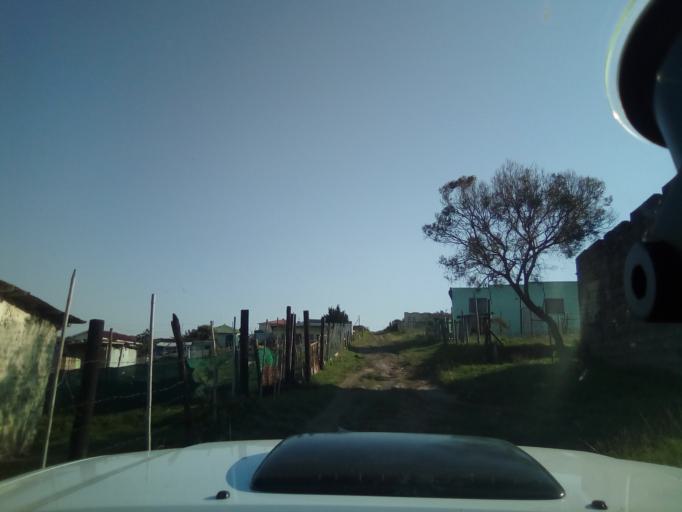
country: ZA
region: Eastern Cape
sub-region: Buffalo City Metropolitan Municipality
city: East London
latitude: -32.8468
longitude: 27.9872
